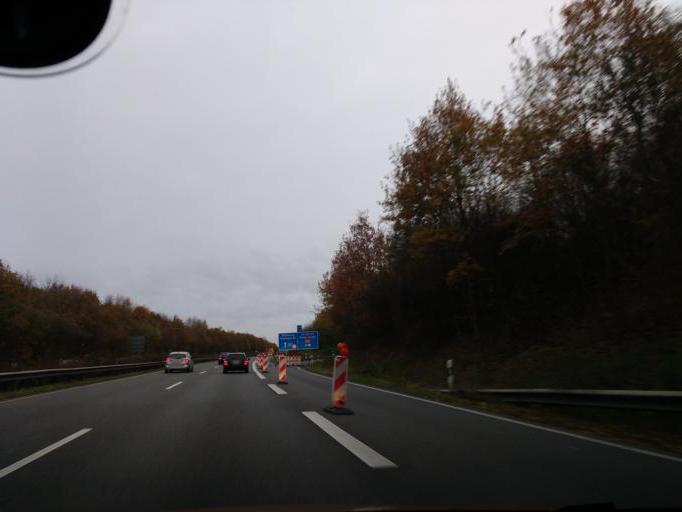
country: DE
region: Lower Saxony
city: Delmenhorst
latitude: 53.0380
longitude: 8.5893
